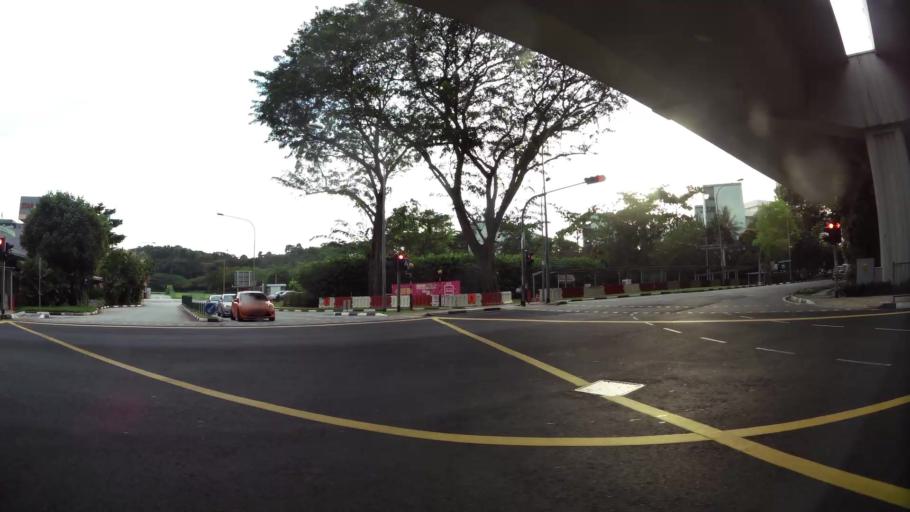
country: SG
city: Singapore
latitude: 1.2727
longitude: 103.8021
